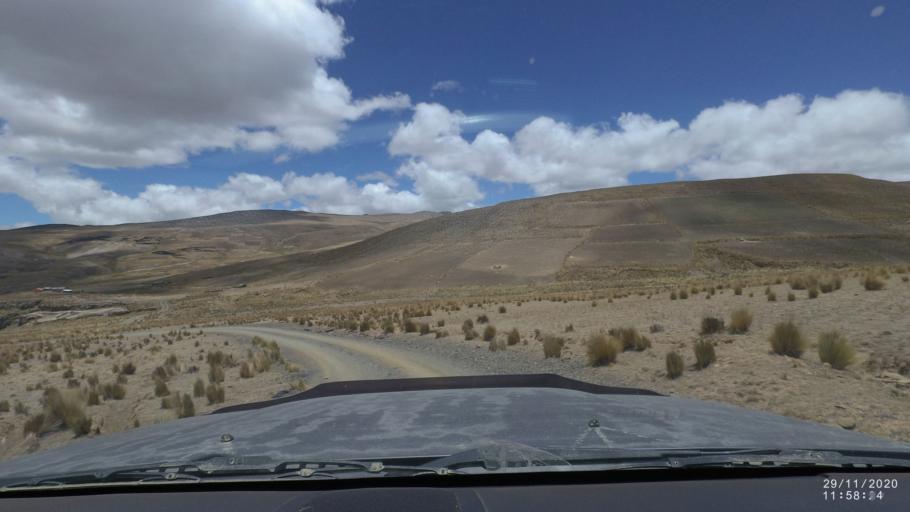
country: BO
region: Cochabamba
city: Cochabamba
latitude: -17.1557
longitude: -66.2746
